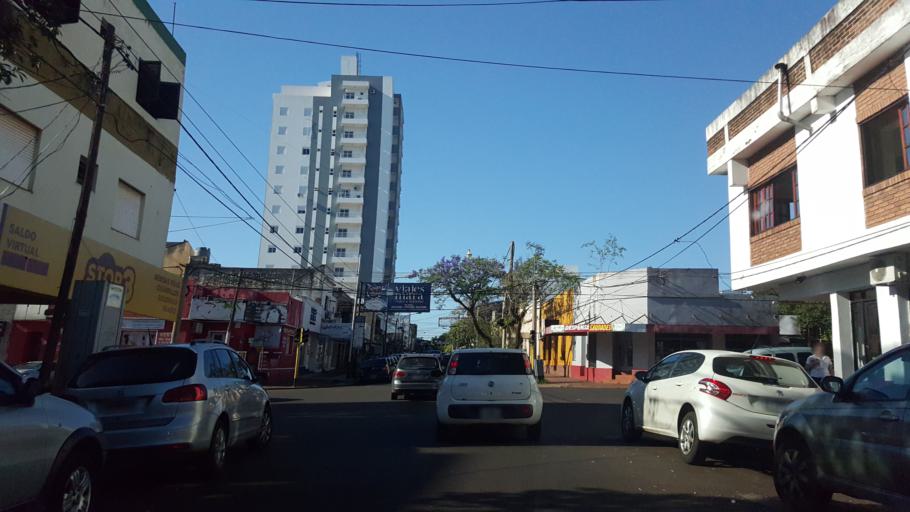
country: AR
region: Misiones
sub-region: Departamento de Capital
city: Posadas
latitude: -27.3712
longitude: -55.8963
